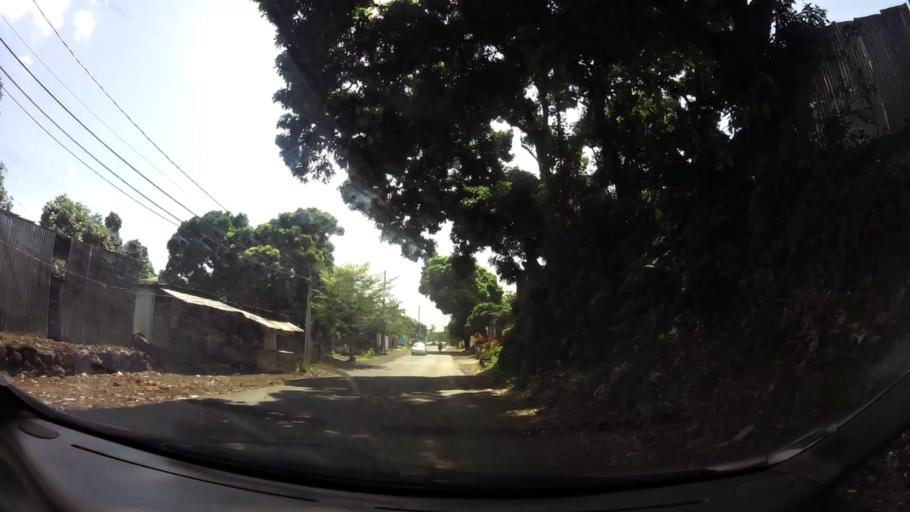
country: KM
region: Grande Comore
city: Mavingouni
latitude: -11.7217
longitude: 43.2506
